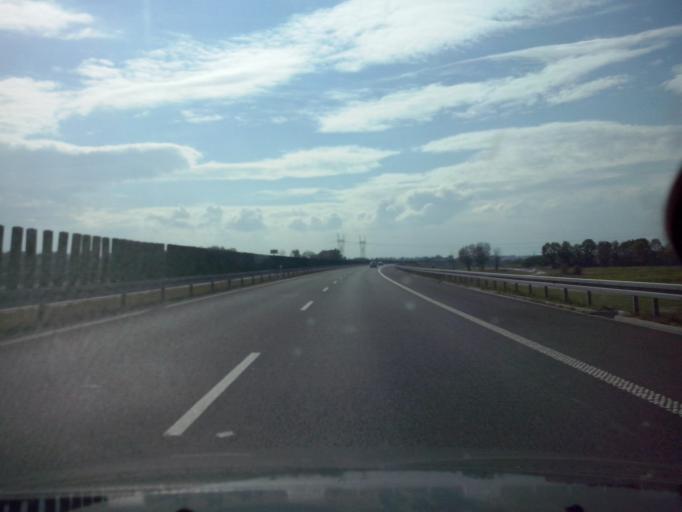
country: PL
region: Lesser Poland Voivodeship
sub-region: Powiat tarnowski
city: Lukowa
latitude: 50.0604
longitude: 20.9501
